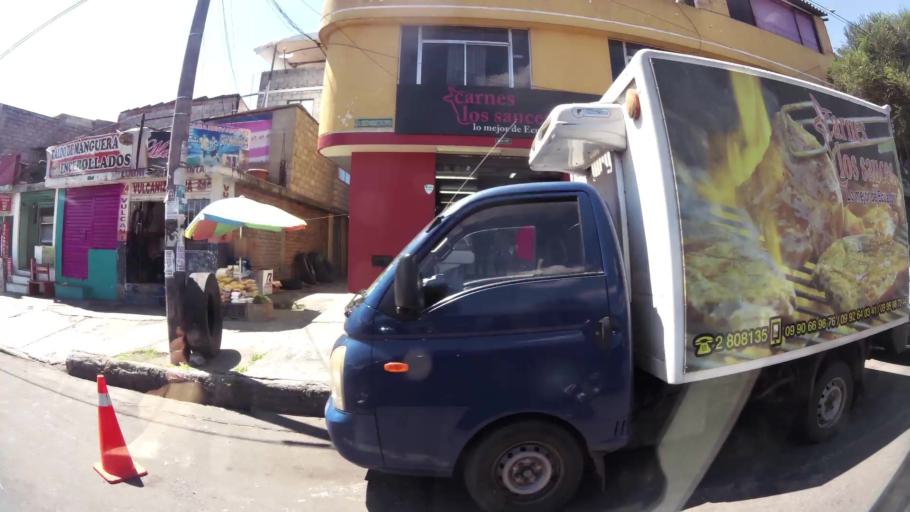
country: EC
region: Pichincha
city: Quito
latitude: -0.1123
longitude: -78.4900
